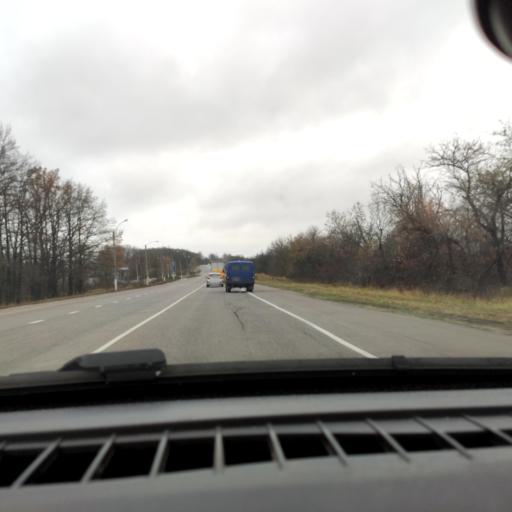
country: RU
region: Voronezj
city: Kolodeznyy
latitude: 51.3315
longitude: 39.0259
